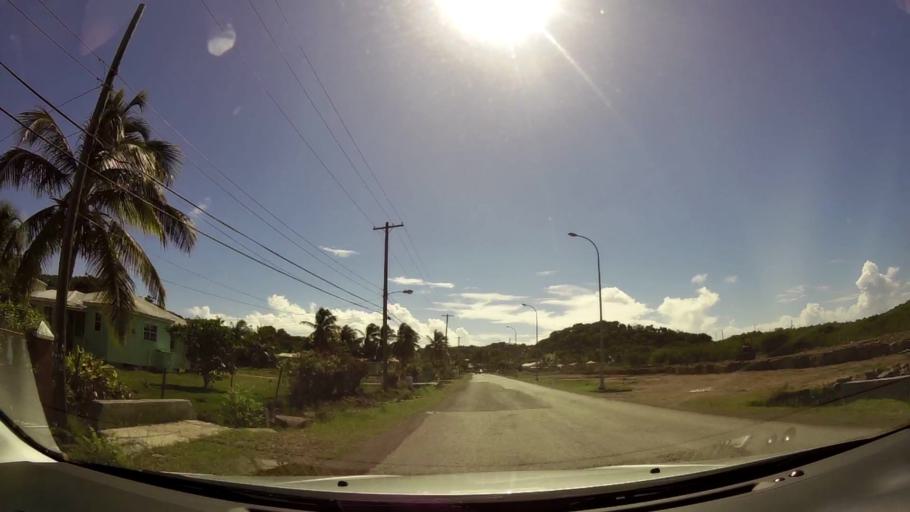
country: AG
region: Saint Paul
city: Falmouth
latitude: 17.0207
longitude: -61.7663
